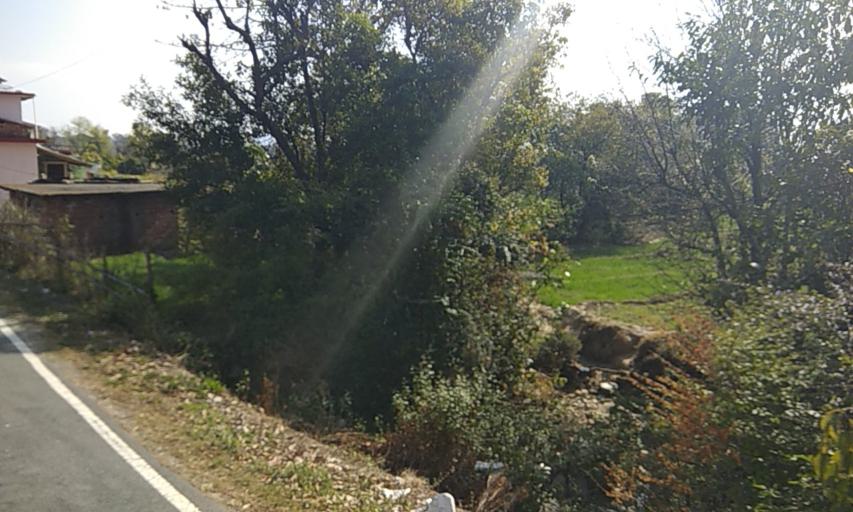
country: IN
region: Himachal Pradesh
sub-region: Kangra
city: Dharmsala
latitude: 32.1576
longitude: 76.4126
